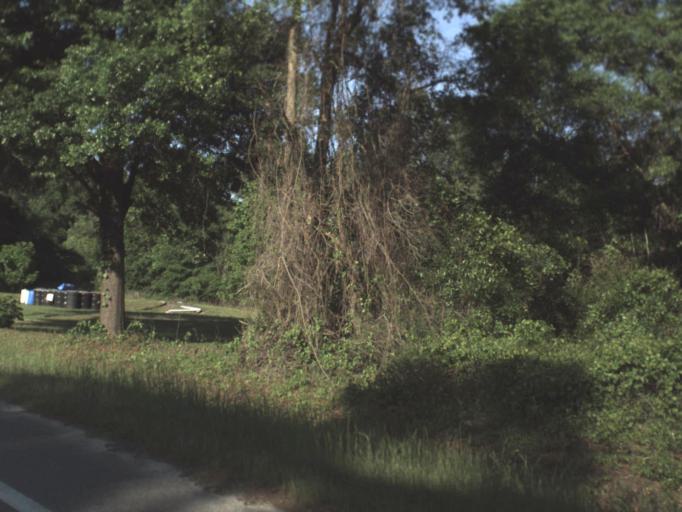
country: US
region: Florida
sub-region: Liberty County
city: Bristol
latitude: 30.3805
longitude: -84.7991
